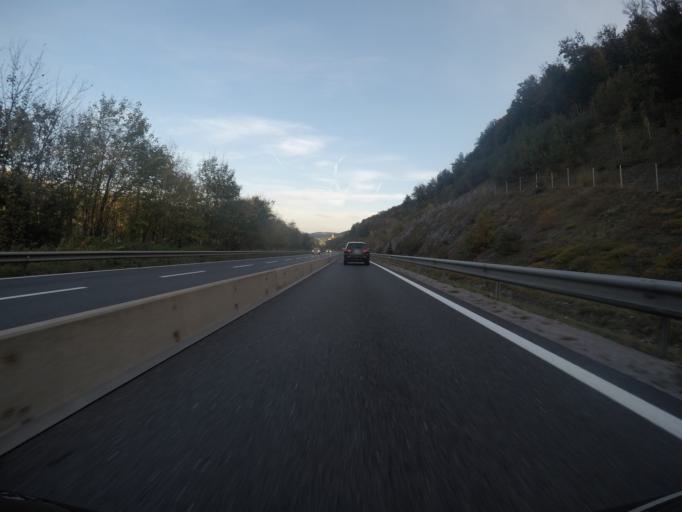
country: SI
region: Grosuplje
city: Grosuplje
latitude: 45.9648
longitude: 14.7288
